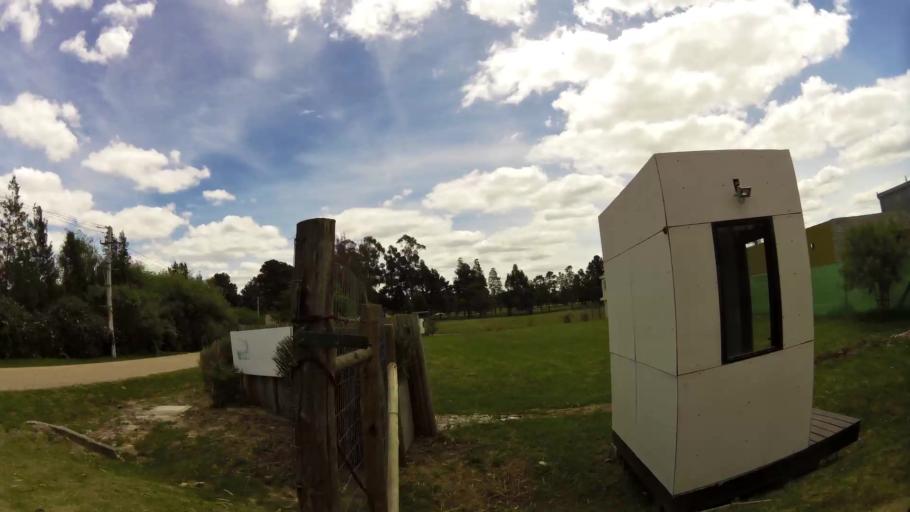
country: UY
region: Canelones
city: Colonia Nicolich
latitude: -34.8166
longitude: -55.9923
